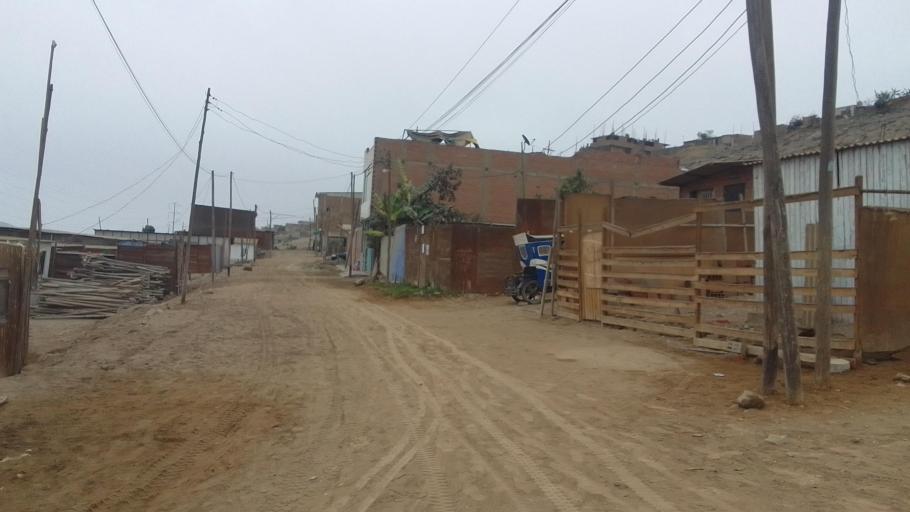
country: PE
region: Lima
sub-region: Lima
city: Santa Rosa
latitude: -11.8149
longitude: -77.1239
